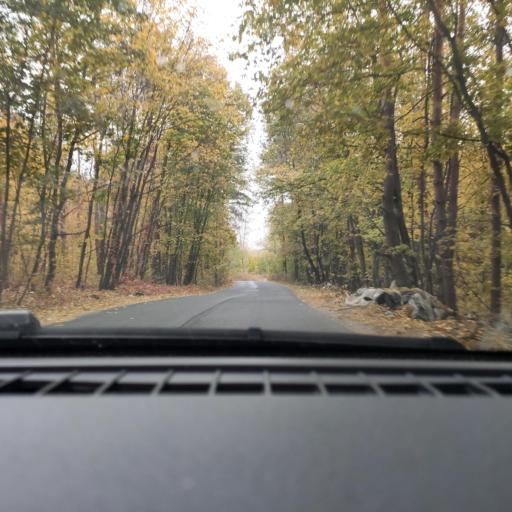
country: RU
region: Voronezj
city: Somovo
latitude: 51.6872
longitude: 39.2984
